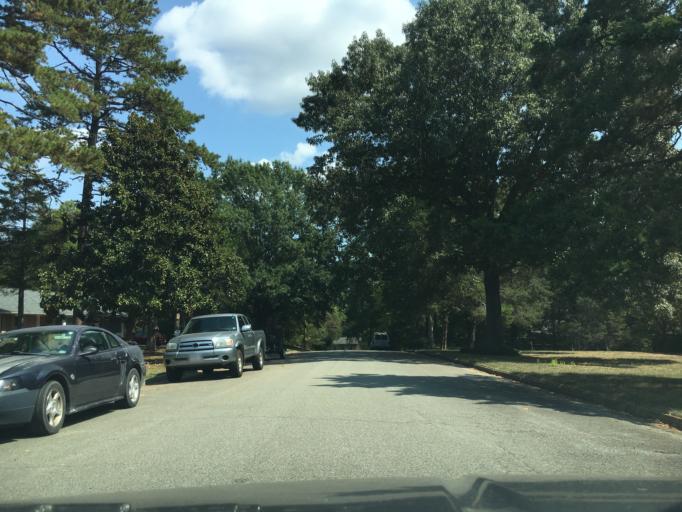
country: US
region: Virginia
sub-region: Halifax County
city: South Boston
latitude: 36.7096
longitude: -78.8950
